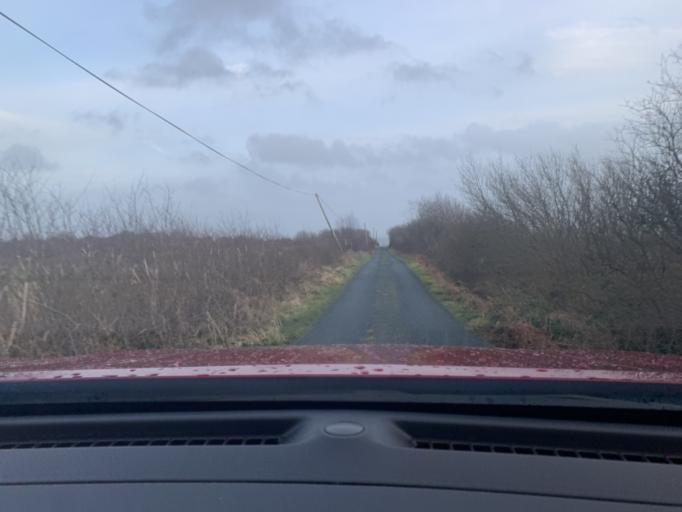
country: IE
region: Connaught
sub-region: Roscommon
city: Ballaghaderreen
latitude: 53.9477
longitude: -8.5091
